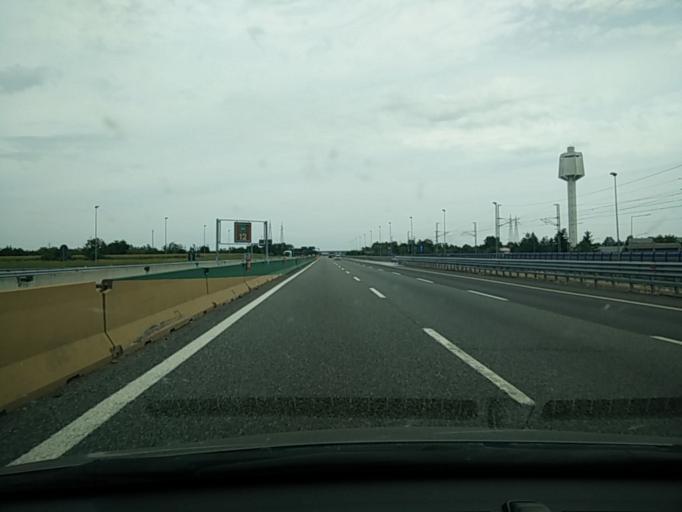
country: IT
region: Piedmont
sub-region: Provincia di Torino
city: Chivasso
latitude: 45.2097
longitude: 7.8901
